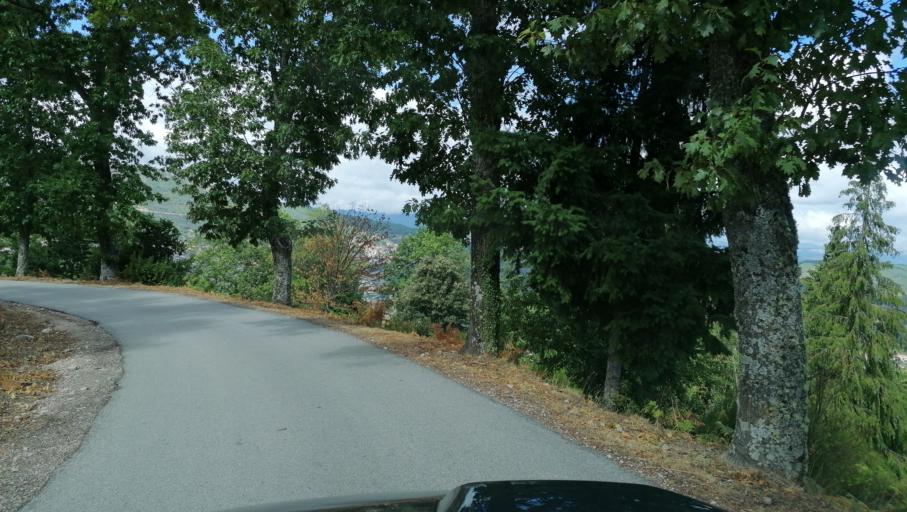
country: PT
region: Vila Real
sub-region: Vila Pouca de Aguiar
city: Vila Pouca de Aguiar
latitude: 41.5352
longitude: -7.5947
